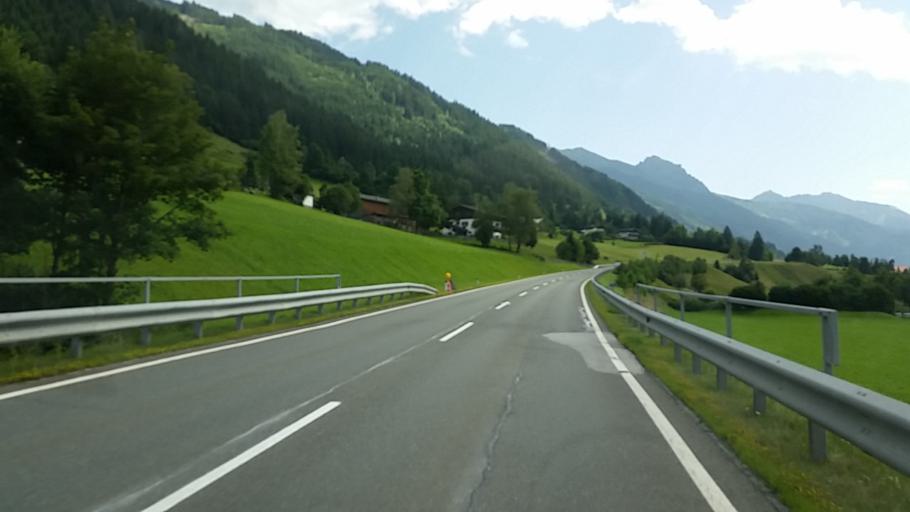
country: AT
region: Salzburg
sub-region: Politischer Bezirk Sankt Johann im Pongau
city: Forstau
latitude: 47.3613
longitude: 13.4941
